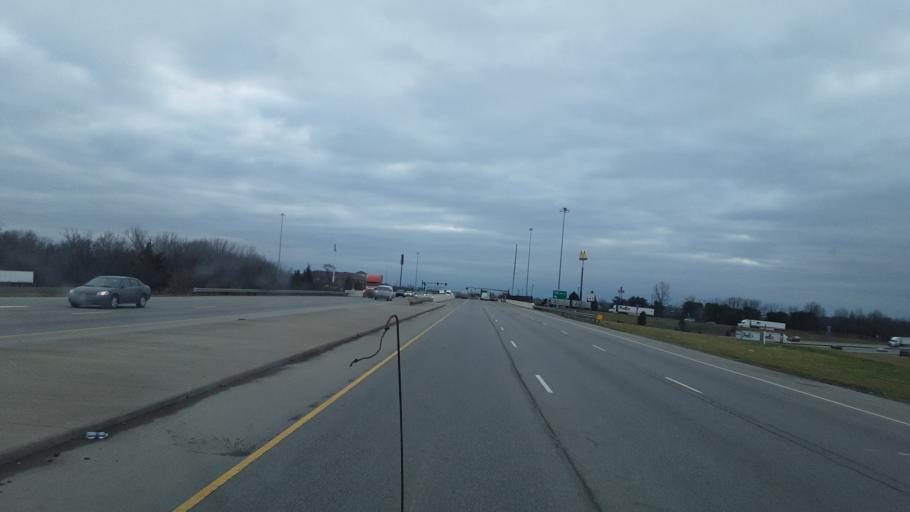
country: US
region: Ohio
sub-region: Franklin County
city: Obetz
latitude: 39.8737
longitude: -82.9328
